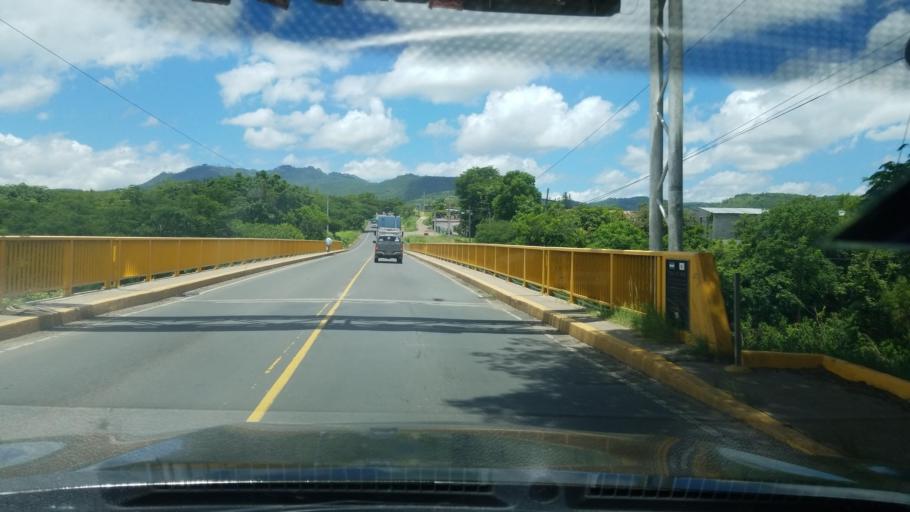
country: HN
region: Francisco Morazan
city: Cofradia
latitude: 14.2664
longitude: -87.2446
